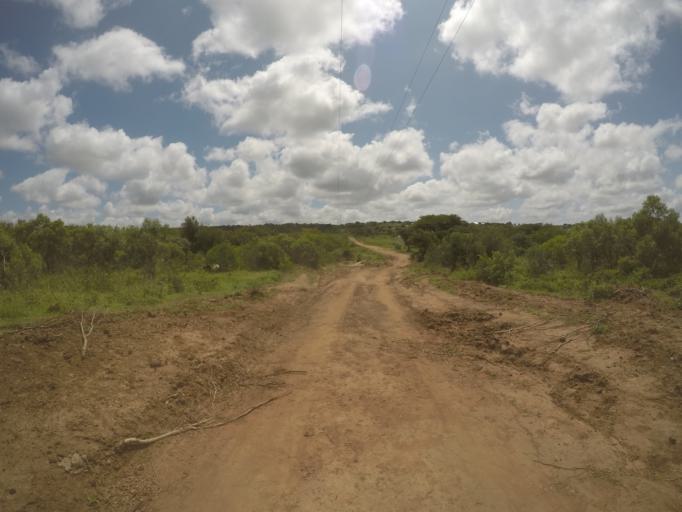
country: ZA
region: KwaZulu-Natal
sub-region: uThungulu District Municipality
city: Empangeni
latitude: -28.5911
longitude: 31.8395
